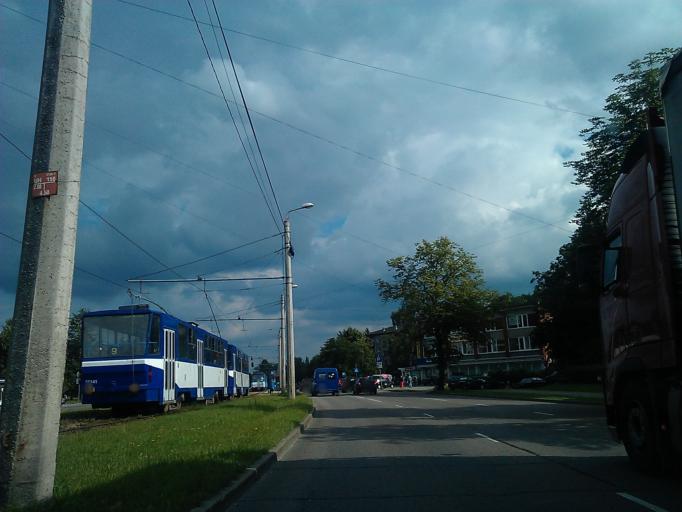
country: LV
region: Kekava
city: Balozi
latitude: 56.9133
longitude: 24.1763
